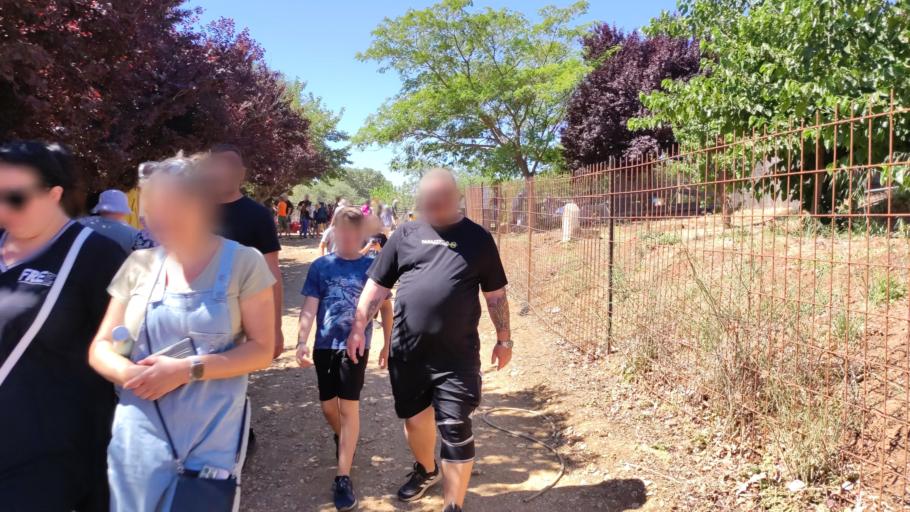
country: SY
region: Quneitra
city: Al Qunaytirah
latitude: 33.1184
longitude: 35.8064
